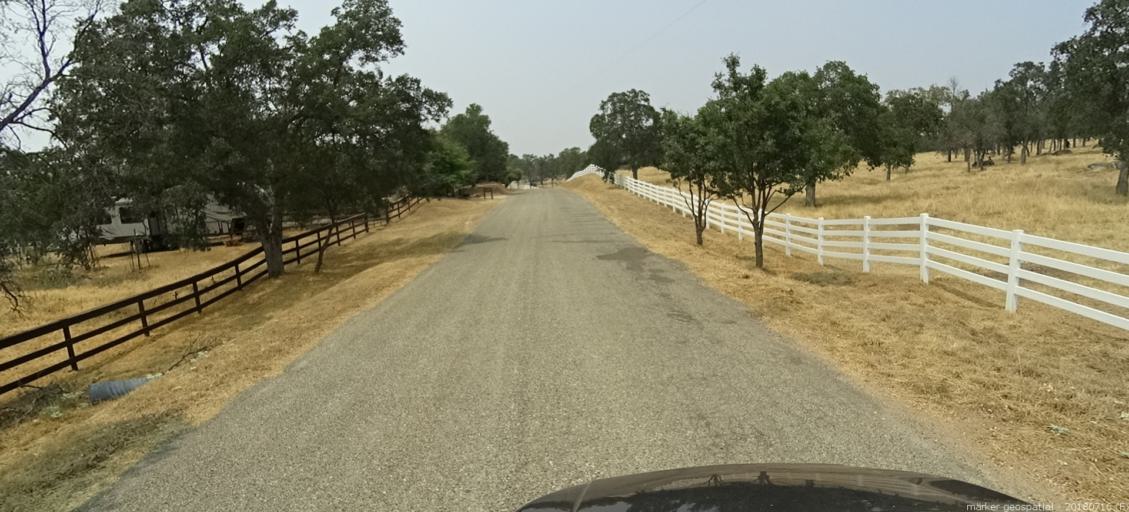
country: US
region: California
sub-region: Madera County
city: Yosemite Lakes
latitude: 37.2374
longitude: -119.8015
